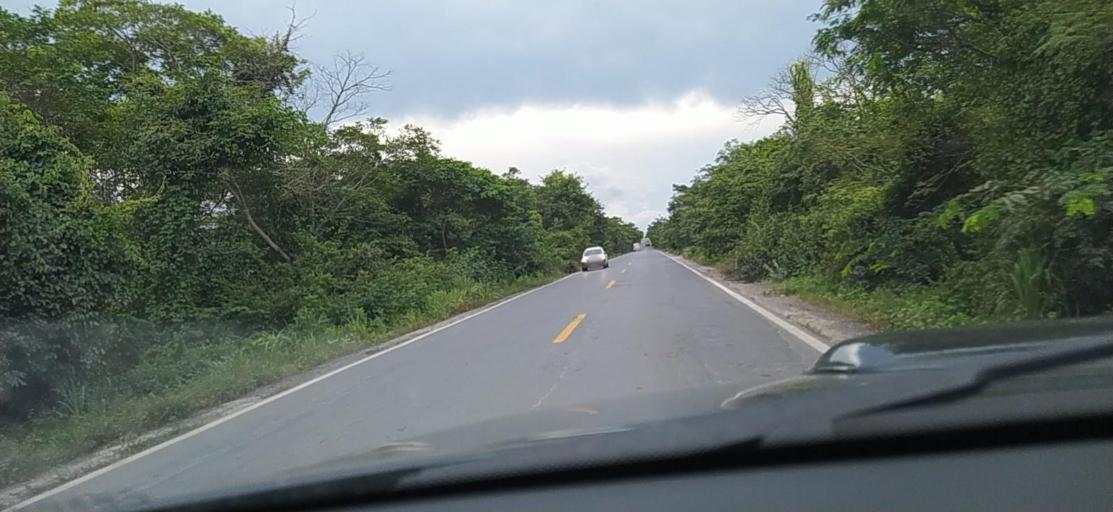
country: BR
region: Minas Gerais
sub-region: Francisco Sa
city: Francisco Sa
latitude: -16.2339
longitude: -43.6166
